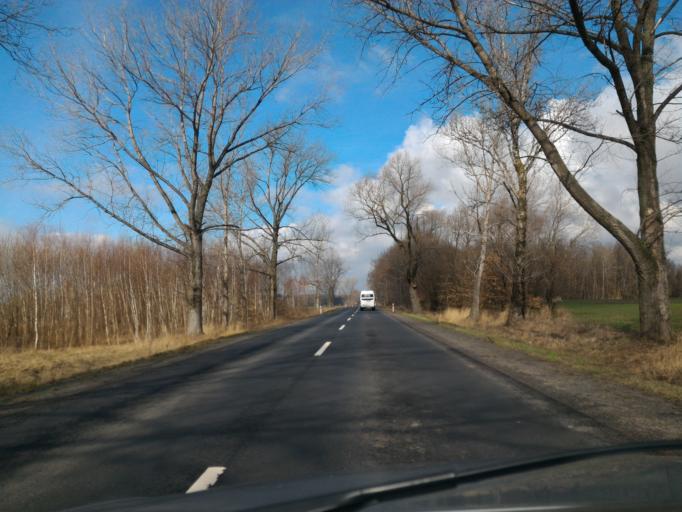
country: PL
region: Silesian Voivodeship
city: Zawidow
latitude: 51.0491
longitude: 15.0424
